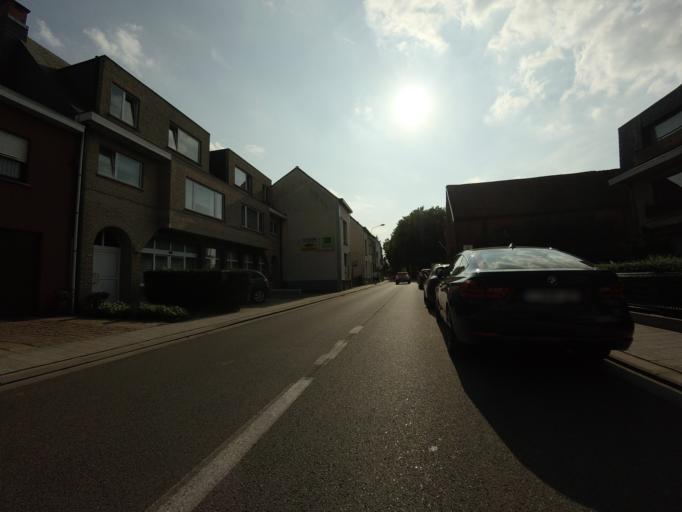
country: BE
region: Flanders
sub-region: Provincie Antwerpen
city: Aartselaar
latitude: 51.1353
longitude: 4.3895
